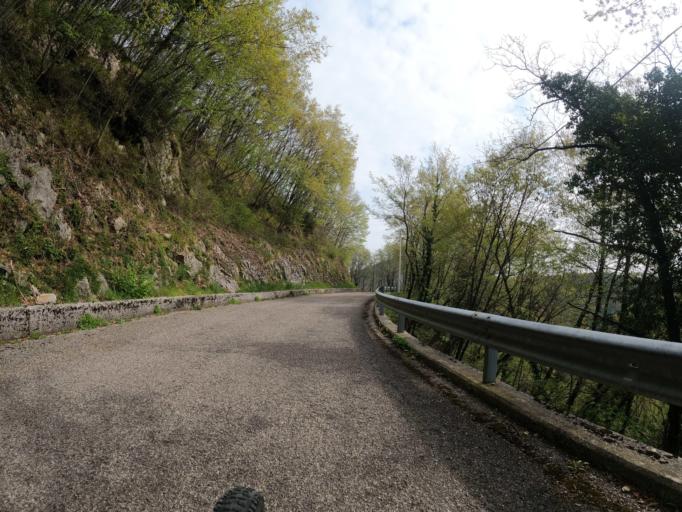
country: IT
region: Friuli Venezia Giulia
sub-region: Provincia di Udine
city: Clodig
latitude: 46.1377
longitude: 13.5990
